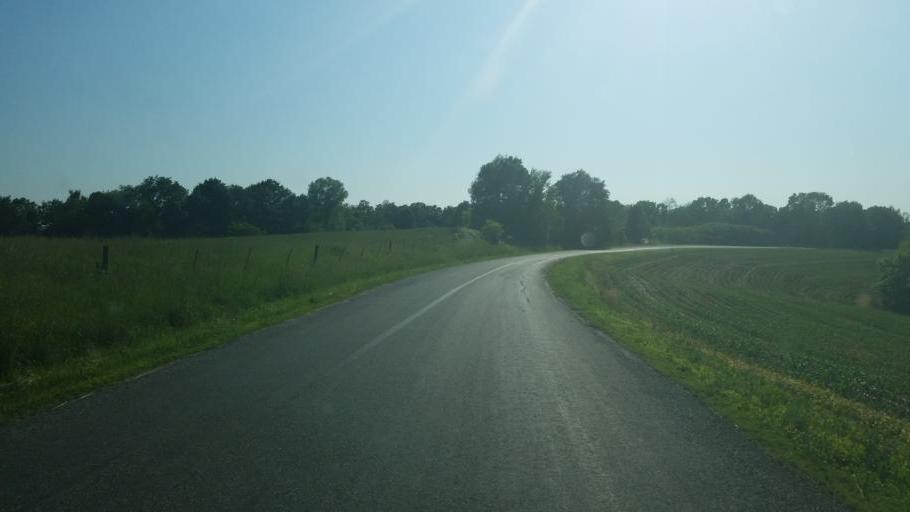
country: US
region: Wisconsin
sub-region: Vernon County
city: Hillsboro
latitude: 43.6754
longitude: -90.3652
